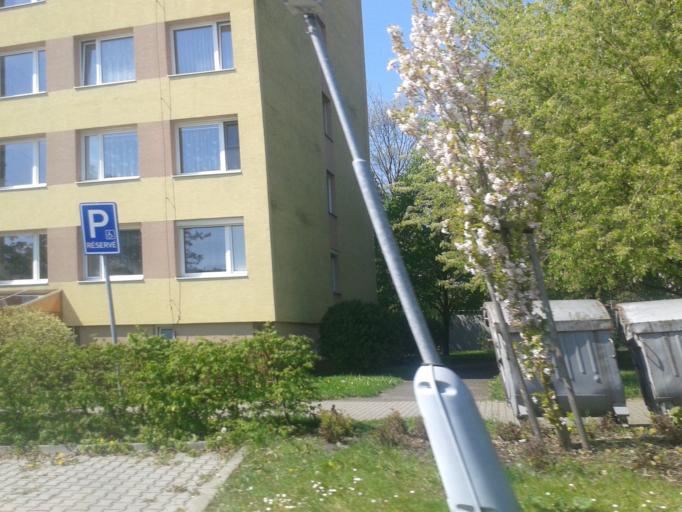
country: CZ
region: Central Bohemia
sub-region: Okres Beroun
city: Kraluv Dvur
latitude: 49.9497
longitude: 14.0372
